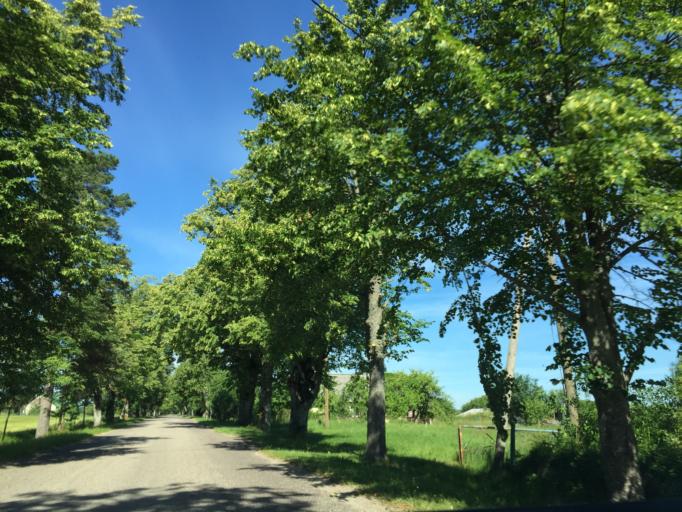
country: LV
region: Kuldigas Rajons
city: Kuldiga
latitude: 57.3246
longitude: 22.0301
